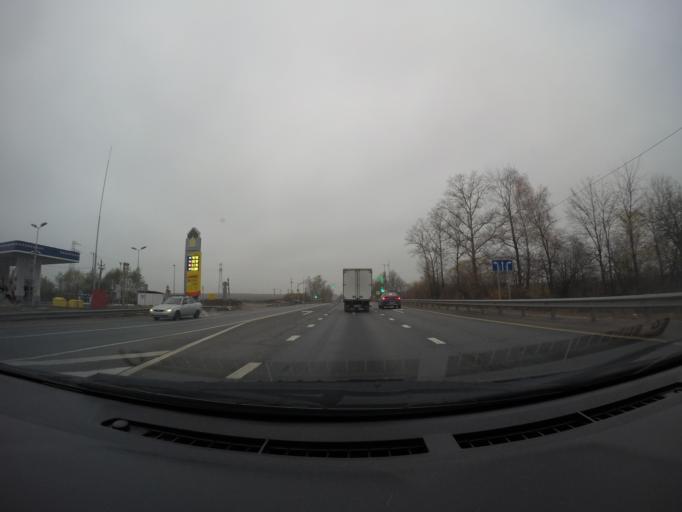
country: RU
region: Moskovskaya
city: Zhitnevo
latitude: 55.3548
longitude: 37.9108
